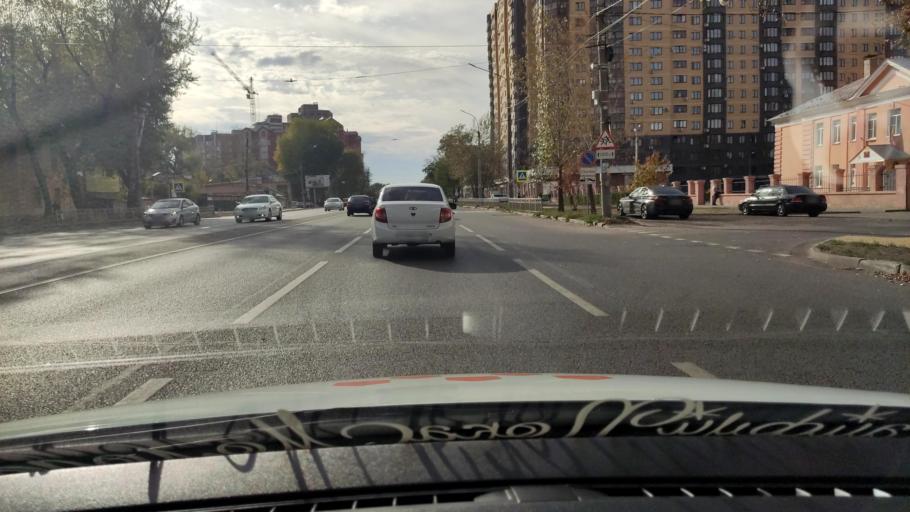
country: RU
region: Voronezj
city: Voronezh
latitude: 51.6744
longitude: 39.1671
